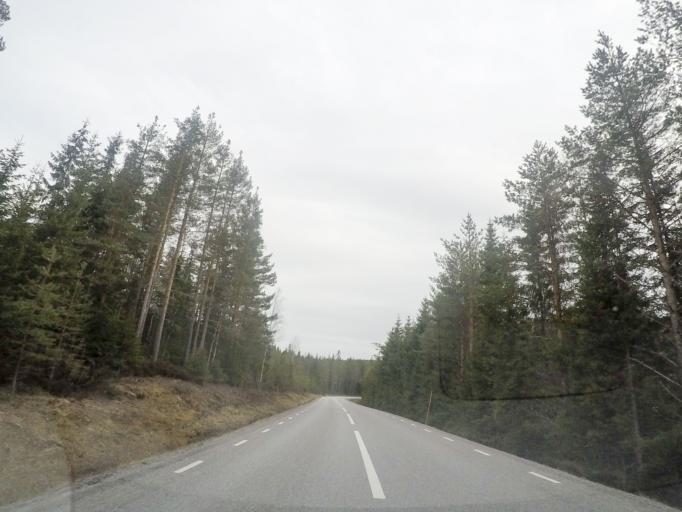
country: SE
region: OErebro
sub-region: Lindesbergs Kommun
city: Stora
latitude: 59.8967
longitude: 15.1875
